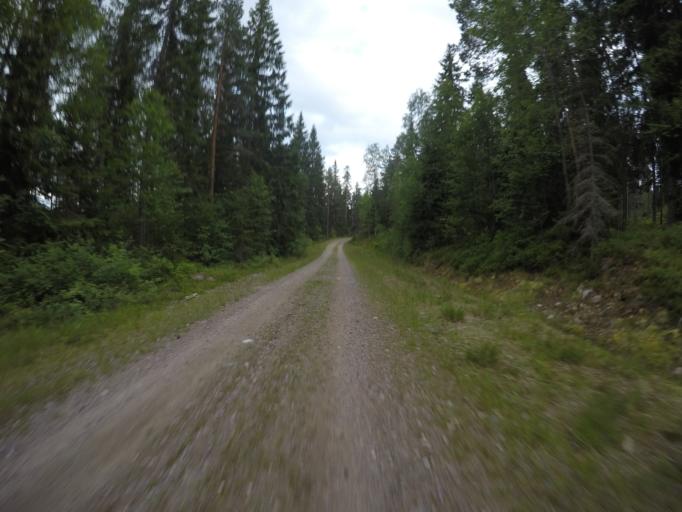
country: SE
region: Vaermland
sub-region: Filipstads Kommun
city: Lesjofors
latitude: 60.1592
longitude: 14.4004
